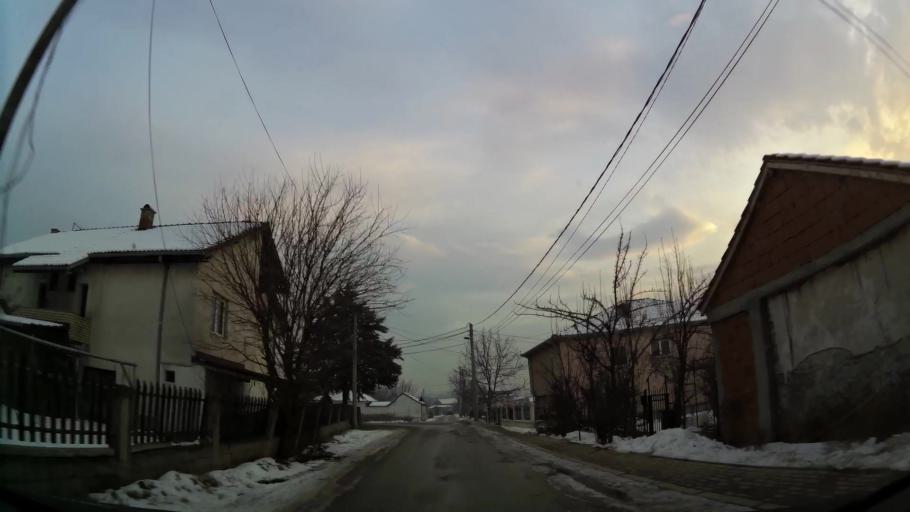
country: MK
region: Suto Orizari
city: Suto Orizare
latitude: 42.0376
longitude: 21.4077
